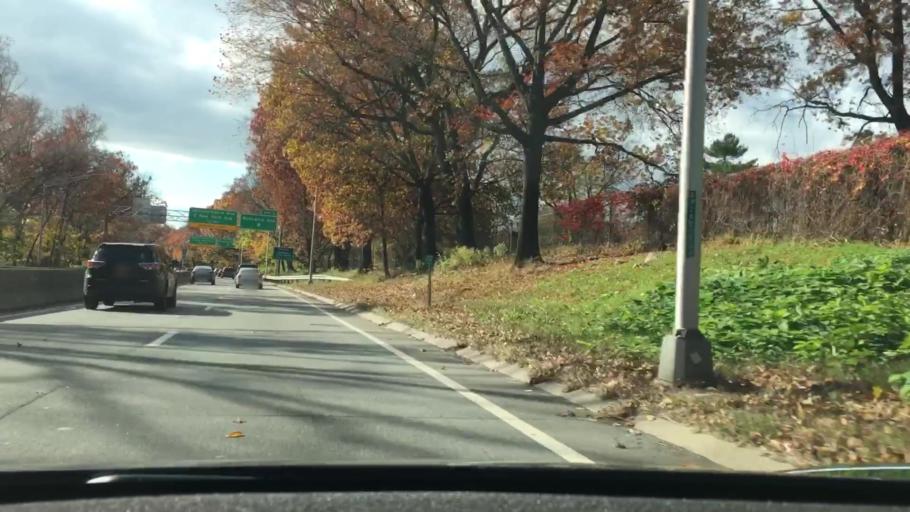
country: US
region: New York
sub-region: Kings County
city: East New York
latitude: 40.6851
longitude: -73.8945
